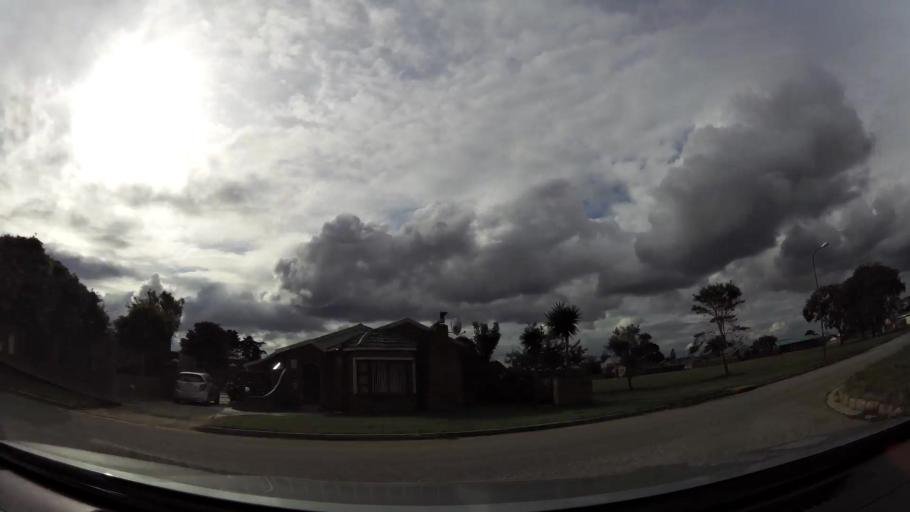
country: ZA
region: Eastern Cape
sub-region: Nelson Mandela Bay Metropolitan Municipality
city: Port Elizabeth
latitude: -33.9379
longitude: 25.5066
